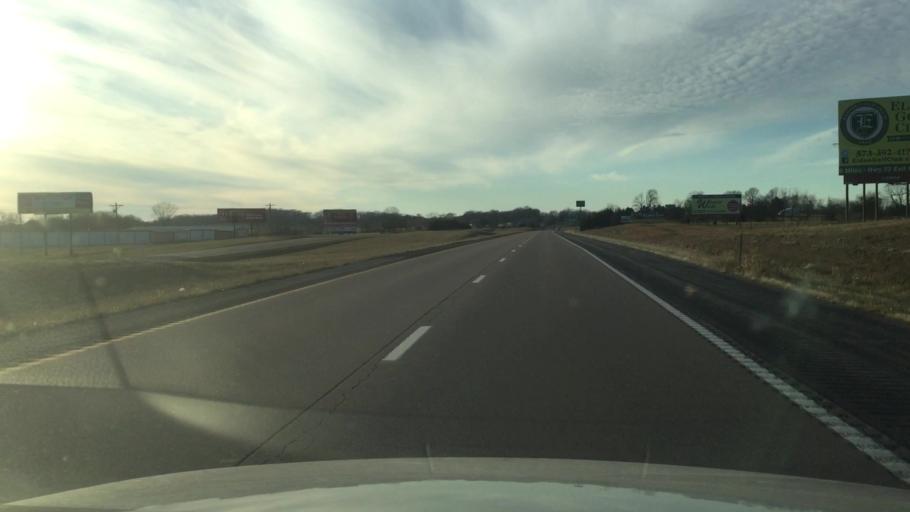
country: US
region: Missouri
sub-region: Miller County
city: Eldon
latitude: 38.3675
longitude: -92.5052
